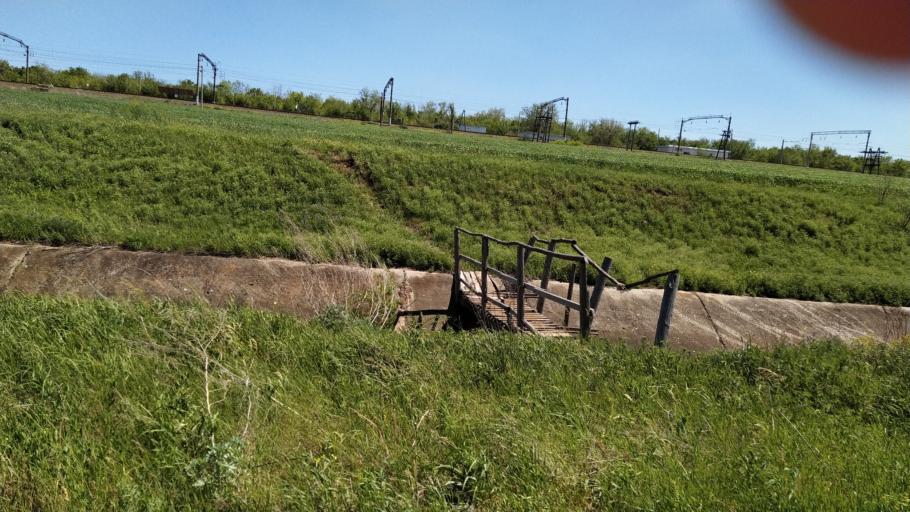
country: RU
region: Rostov
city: Kuleshovka
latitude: 47.0348
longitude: 39.6375
